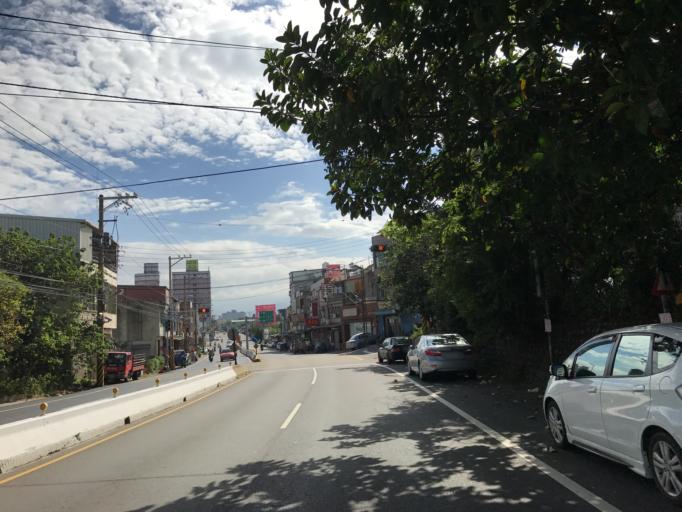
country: TW
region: Taiwan
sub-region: Hsinchu
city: Zhubei
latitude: 24.7728
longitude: 121.0492
